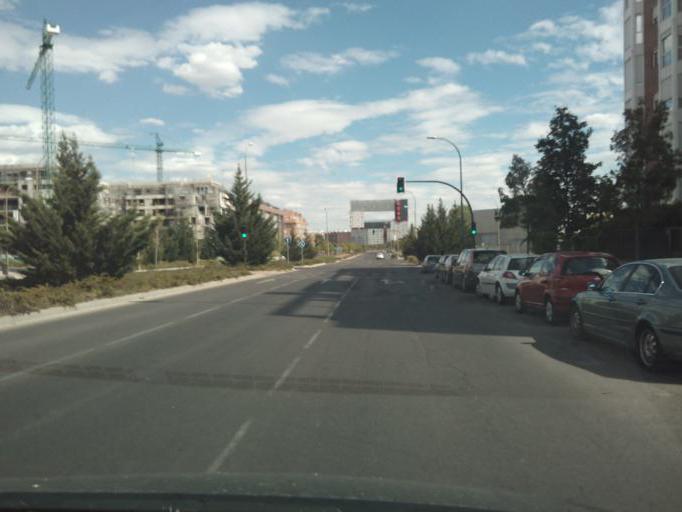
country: ES
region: Madrid
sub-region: Provincia de Madrid
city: Pinar de Chamartin
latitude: 40.4919
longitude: -3.6616
